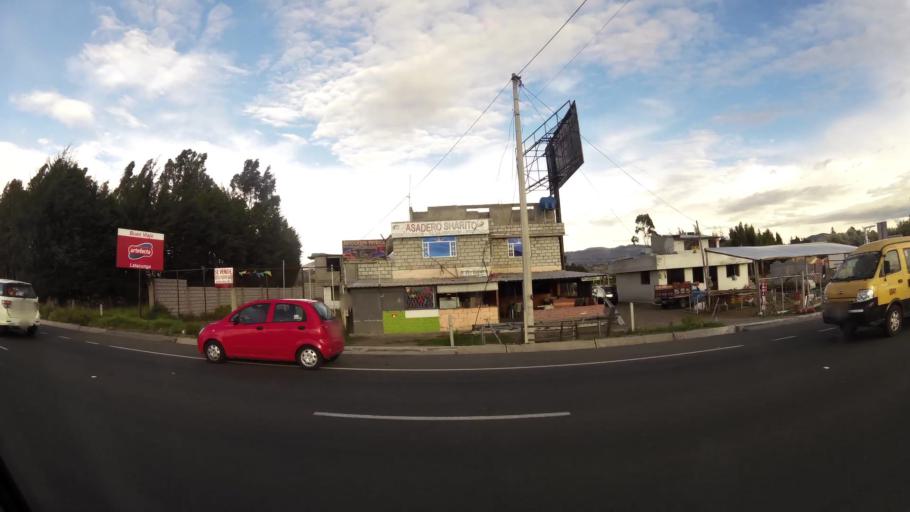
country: EC
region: Cotopaxi
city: Saquisili
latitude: -0.8748
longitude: -78.6275
